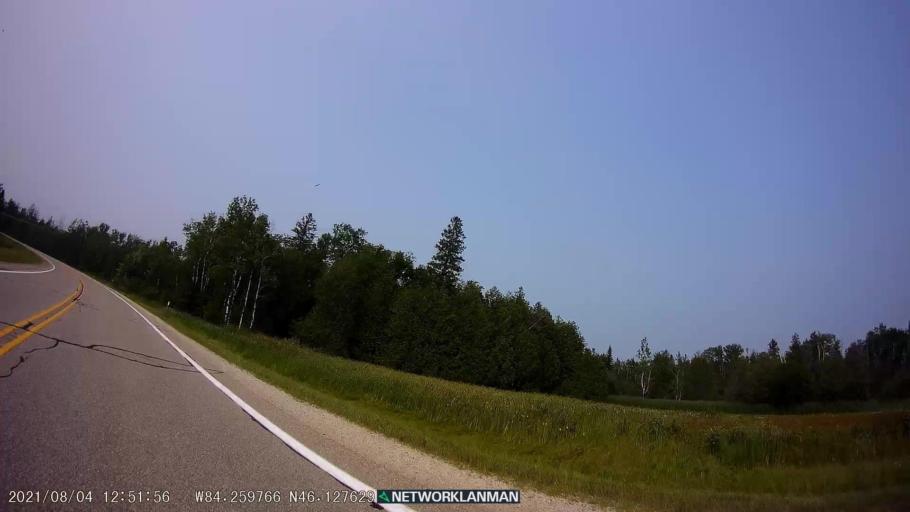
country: US
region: Michigan
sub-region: Chippewa County
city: Sault Ste. Marie
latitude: 46.1276
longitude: -84.2596
